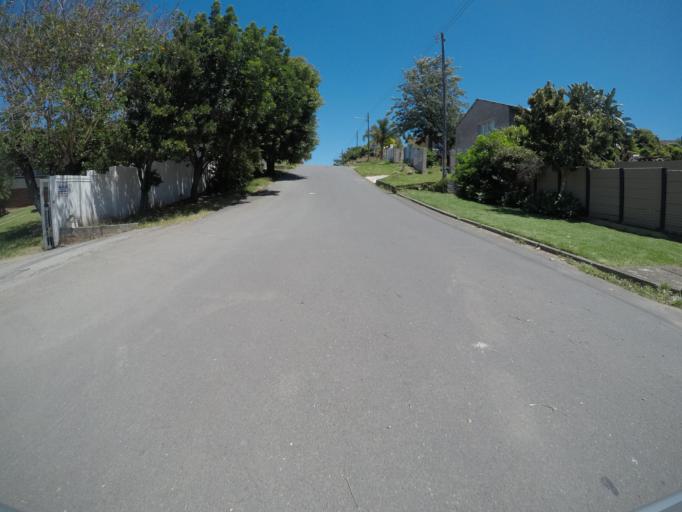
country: ZA
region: Eastern Cape
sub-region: Buffalo City Metropolitan Municipality
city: East London
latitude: -32.9604
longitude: 27.9366
